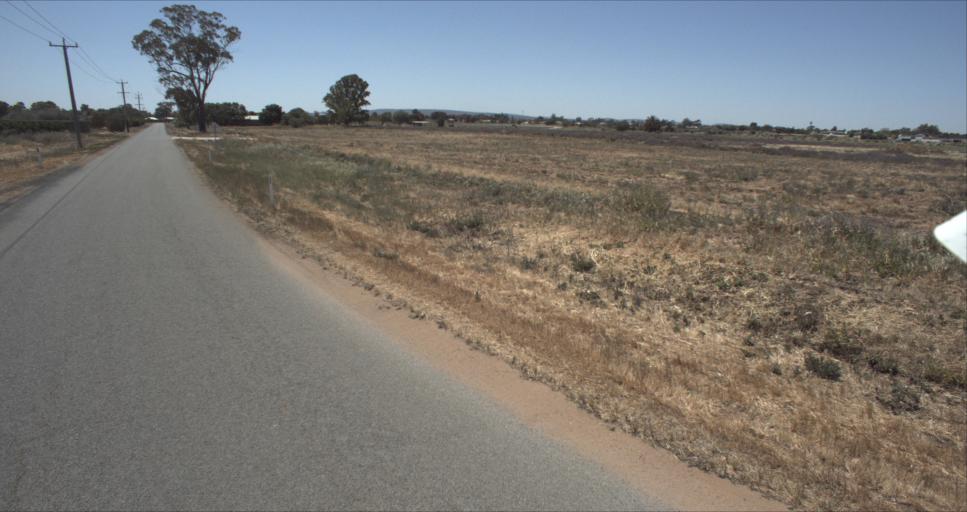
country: AU
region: New South Wales
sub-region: Leeton
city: Leeton
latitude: -34.5373
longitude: 146.3957
